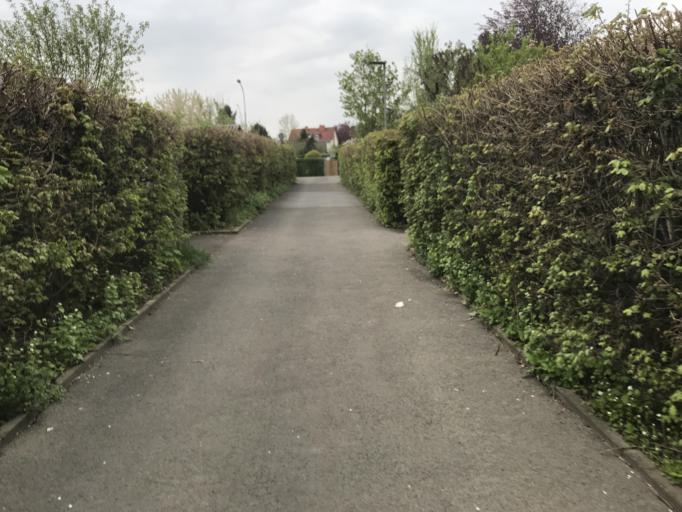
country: DE
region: Hesse
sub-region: Regierungsbezirk Giessen
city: Giessen
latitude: 50.5948
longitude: 8.6878
